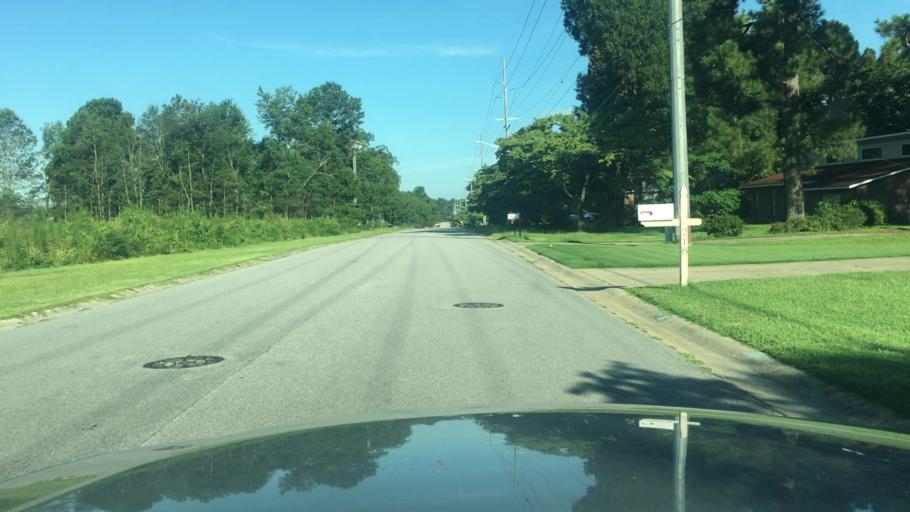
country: US
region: North Carolina
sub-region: Cumberland County
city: Fayetteville
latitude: 35.1290
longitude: -78.8827
